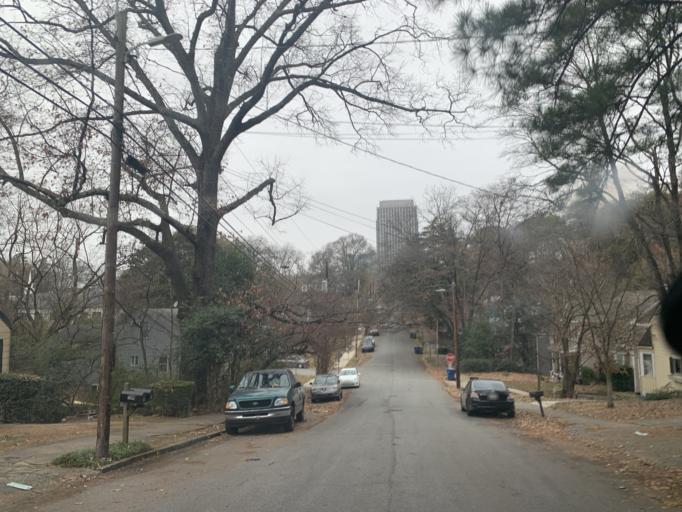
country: US
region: Georgia
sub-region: Fulton County
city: Atlanta
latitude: 33.7836
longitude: -84.3977
